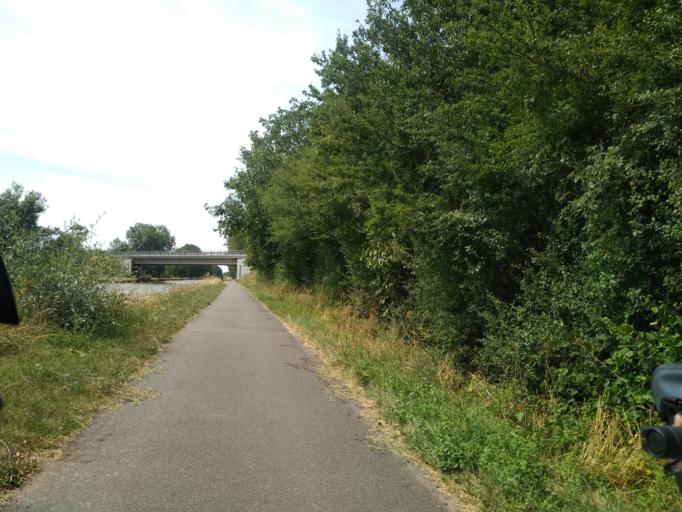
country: FR
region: Auvergne
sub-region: Departement de l'Allier
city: Diou
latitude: 46.5120
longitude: 3.8029
